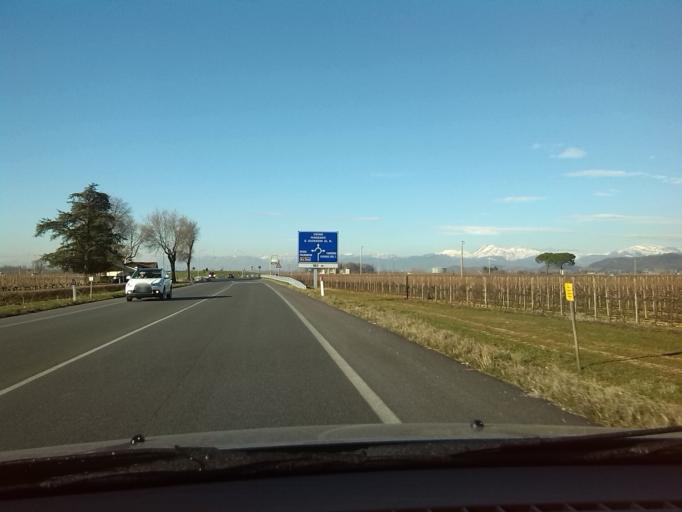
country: IT
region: Friuli Venezia Giulia
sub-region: Provincia di Gorizia
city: Mariano del Friuli
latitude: 45.9326
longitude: 13.4516
